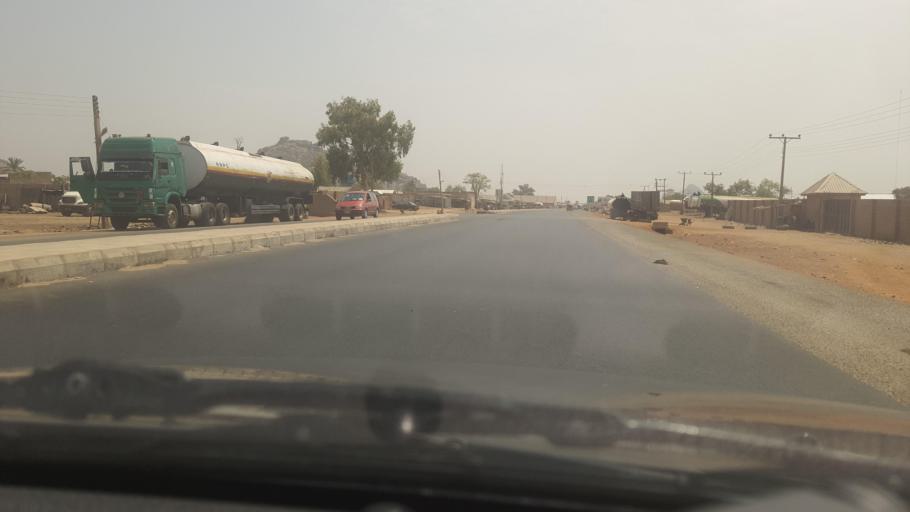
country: NG
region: Bauchi
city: Bauchi
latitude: 10.3039
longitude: 9.7422
